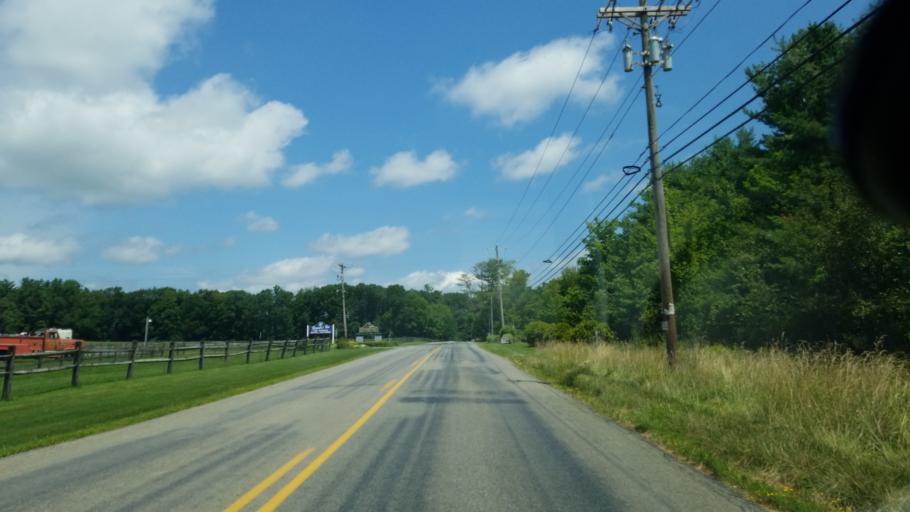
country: US
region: Pennsylvania
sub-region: Jefferson County
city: Brookville
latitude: 41.2979
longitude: -79.0920
